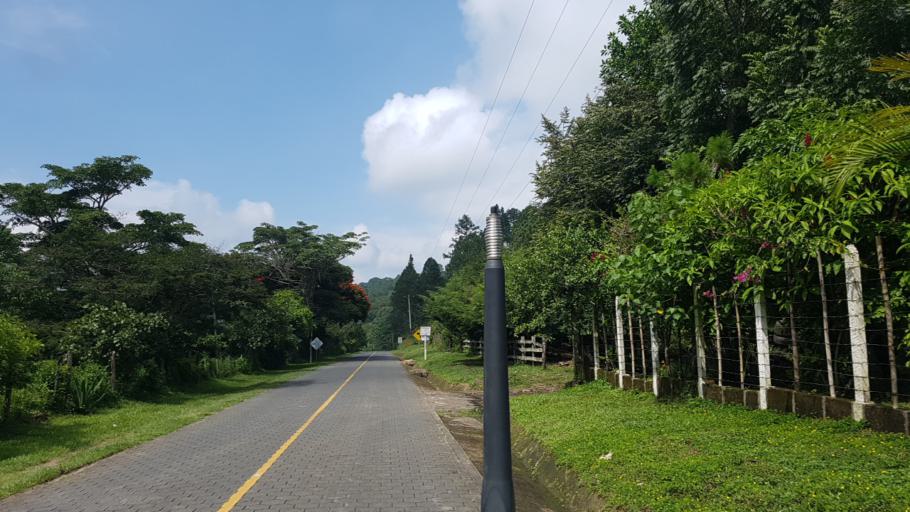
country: NI
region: Esteli
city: Esteli
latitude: 12.9733
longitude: -86.3364
